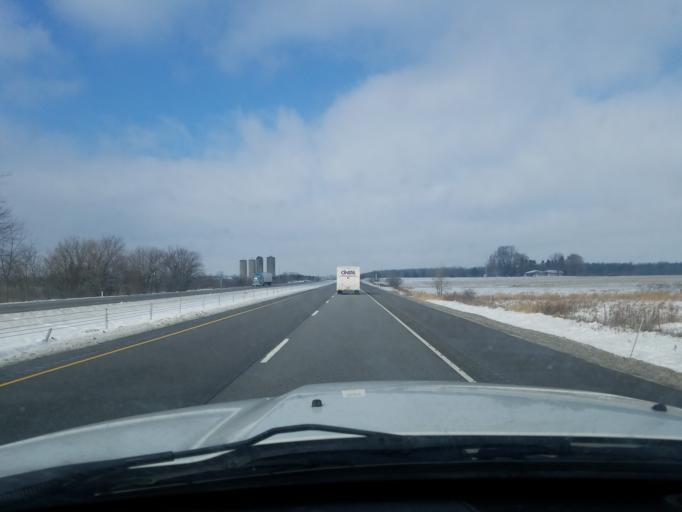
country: US
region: Indiana
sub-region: Marshall County
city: Plymouth
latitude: 41.3974
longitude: -86.2900
